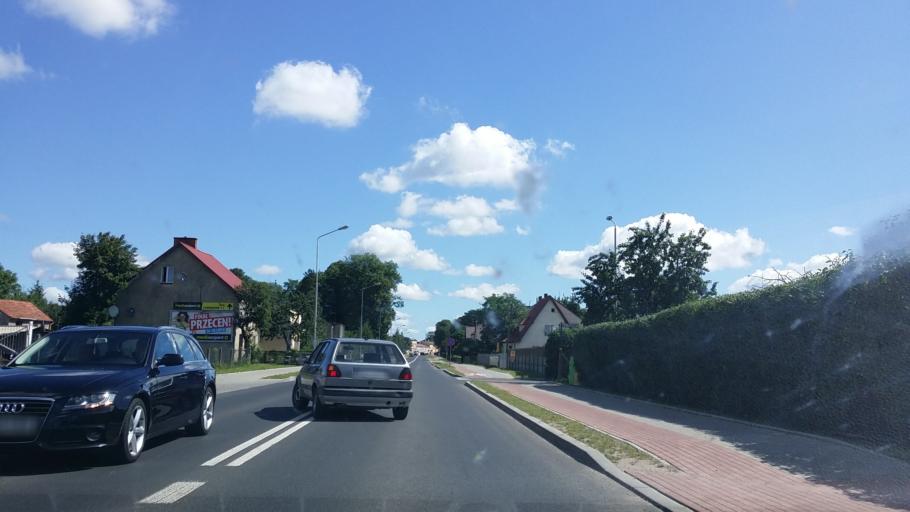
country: PL
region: West Pomeranian Voivodeship
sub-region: Powiat drawski
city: Drawsko Pomorskie
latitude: 53.5275
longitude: 15.7980
